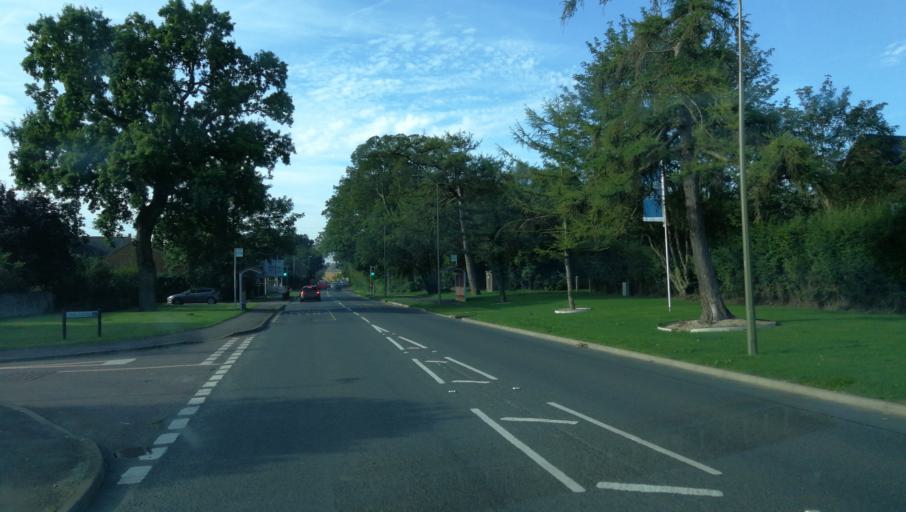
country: GB
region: England
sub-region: Oxfordshire
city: Deddington
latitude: 51.9843
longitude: -1.3227
